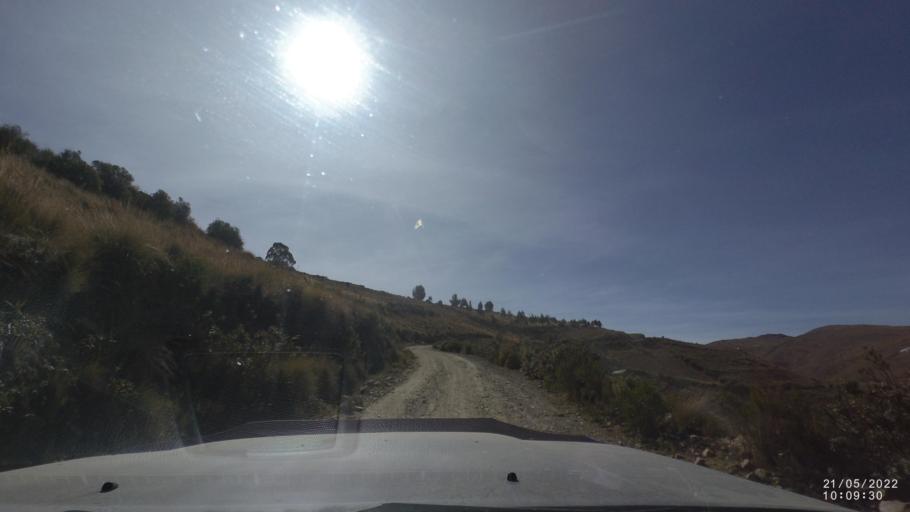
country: BO
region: Cochabamba
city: Colomi
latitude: -17.3366
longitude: -65.9862
